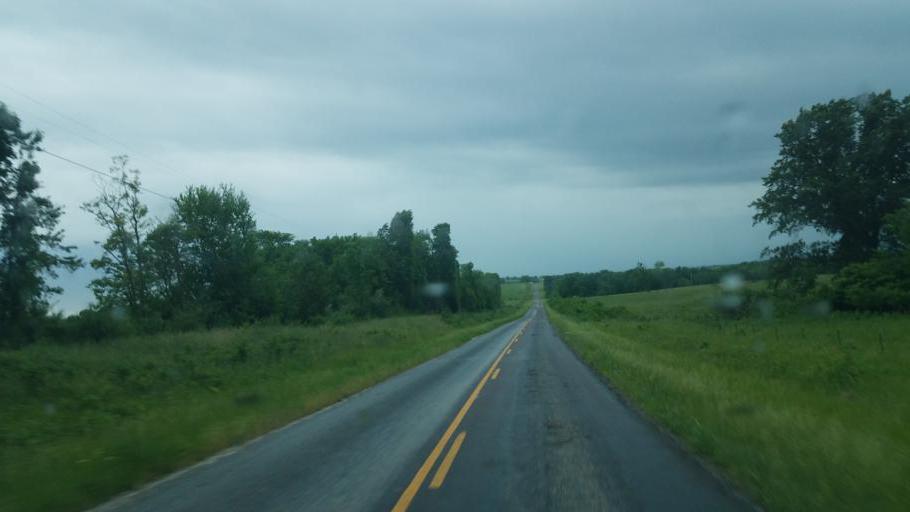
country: US
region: Missouri
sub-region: Moniteau County
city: California
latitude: 38.7814
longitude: -92.6050
